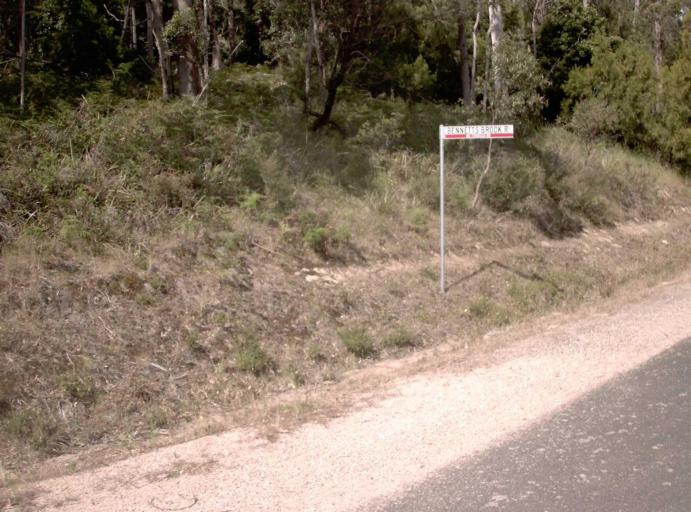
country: AU
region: Victoria
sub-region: East Gippsland
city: Lakes Entrance
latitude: -37.8252
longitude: 147.8873
